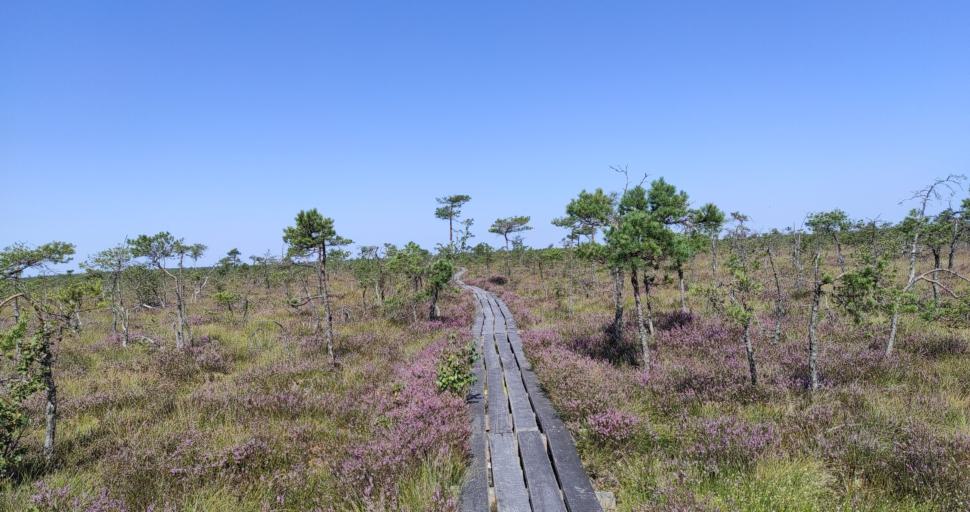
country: LT
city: Skuodas
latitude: 56.2499
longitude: 21.3953
